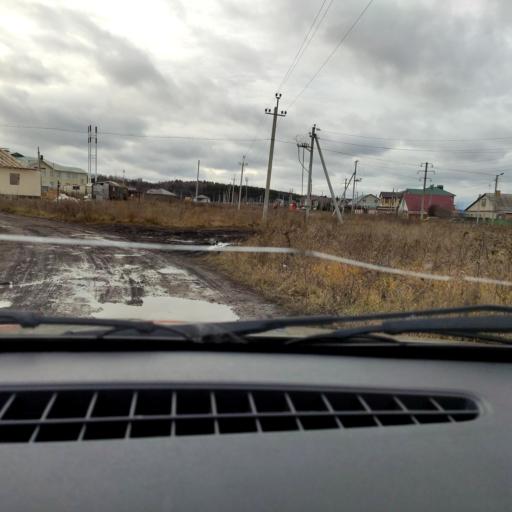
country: RU
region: Bashkortostan
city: Avdon
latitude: 54.4874
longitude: 55.8567
